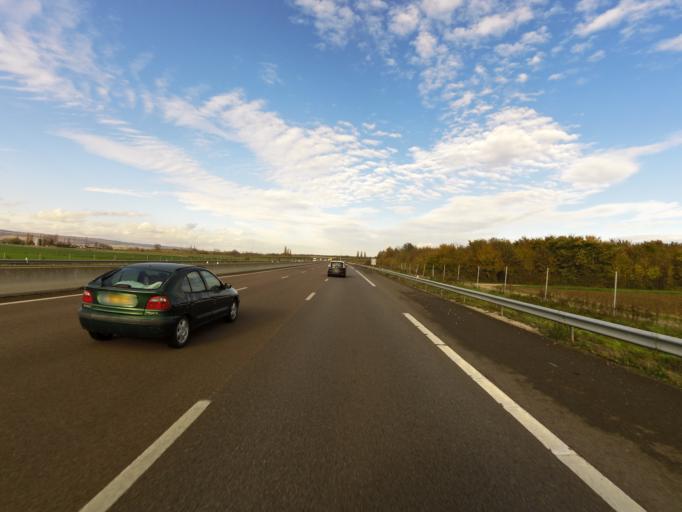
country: FR
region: Bourgogne
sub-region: Departement de la Cote-d'Or
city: Nuits-Saint-Georges
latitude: 47.1592
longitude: 4.9980
